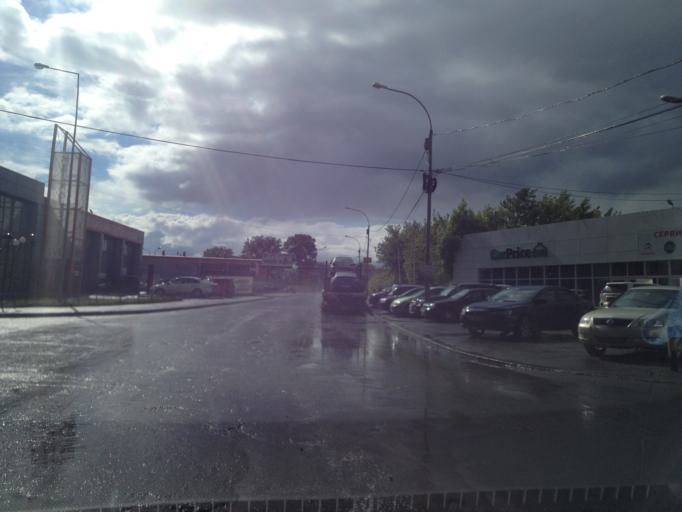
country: RU
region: Sverdlovsk
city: Yekaterinburg
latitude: 56.8626
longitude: 60.6076
